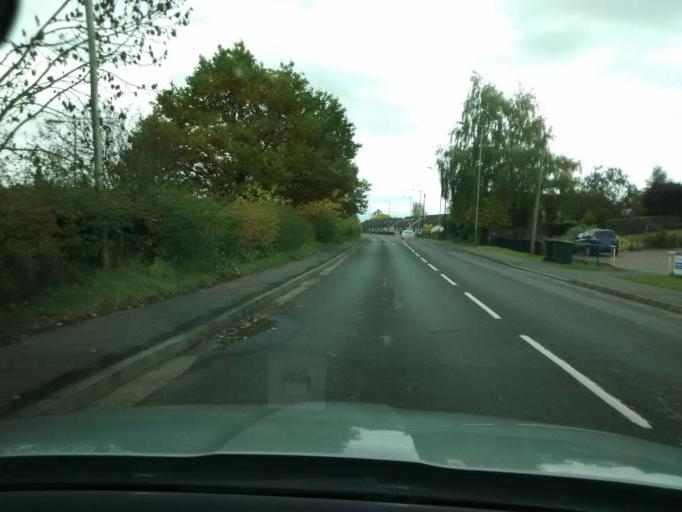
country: GB
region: Scotland
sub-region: Perth and Kinross
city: Luncarty
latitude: 56.4515
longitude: -3.4705
